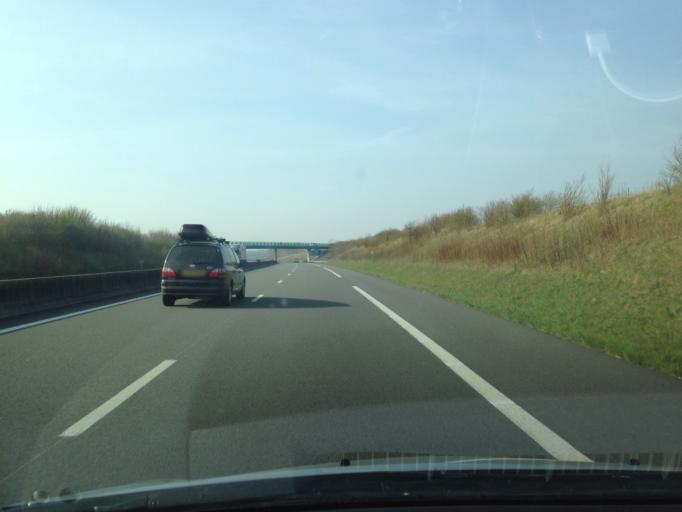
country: FR
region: Picardie
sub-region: Departement de la Somme
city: Nouvion
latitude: 50.2606
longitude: 1.7462
